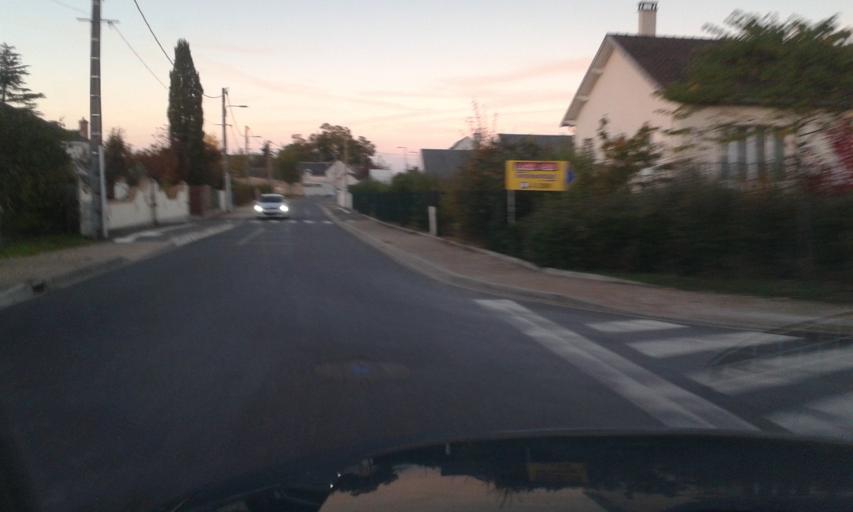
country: FR
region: Centre
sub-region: Departement du Loiret
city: Olivet
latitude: 47.8597
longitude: 1.8808
